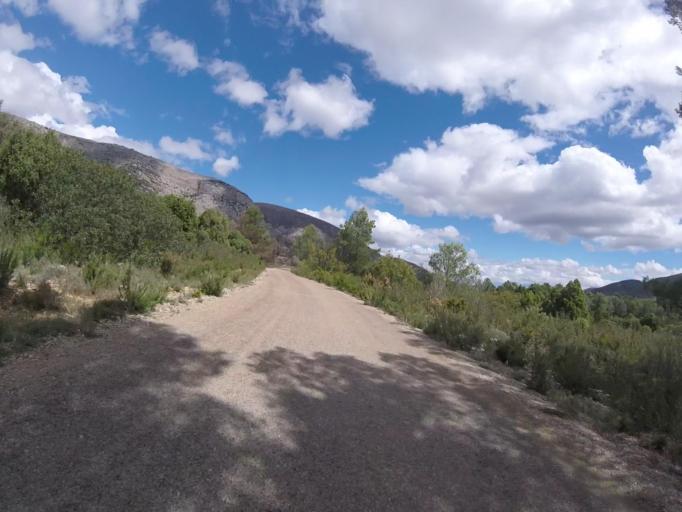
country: ES
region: Valencia
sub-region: Provincia de Castello
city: Sierra-Engarceran
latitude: 40.2872
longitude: -0.0646
